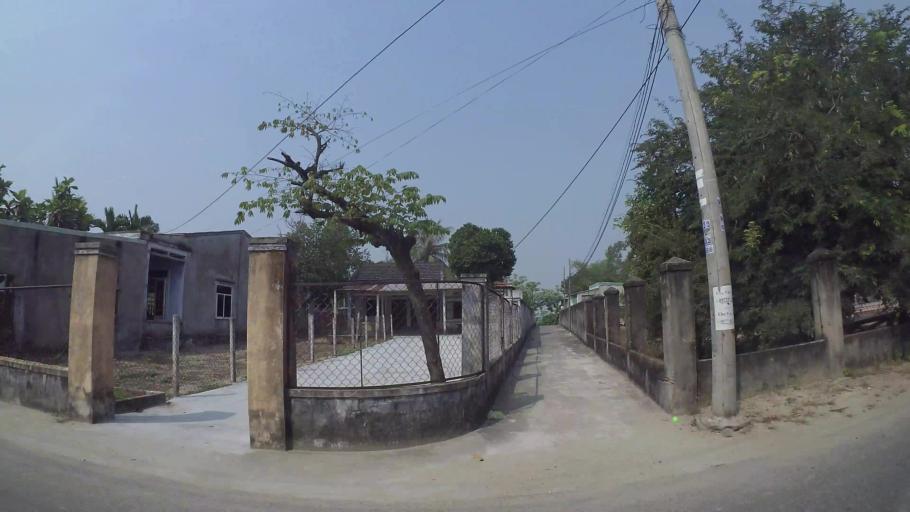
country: VN
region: Da Nang
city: Ngu Hanh Son
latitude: 15.9900
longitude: 108.2404
